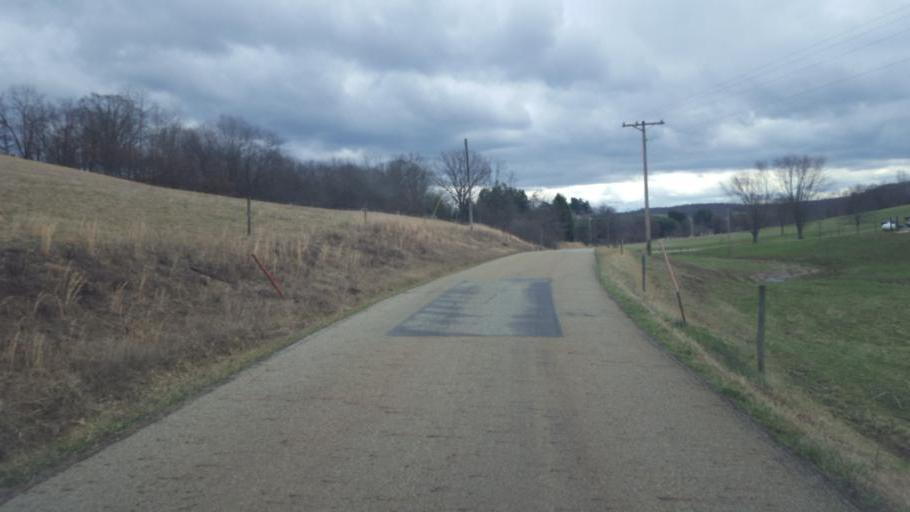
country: US
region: Ohio
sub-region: Muskingum County
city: Frazeysburg
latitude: 40.1381
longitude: -82.2336
